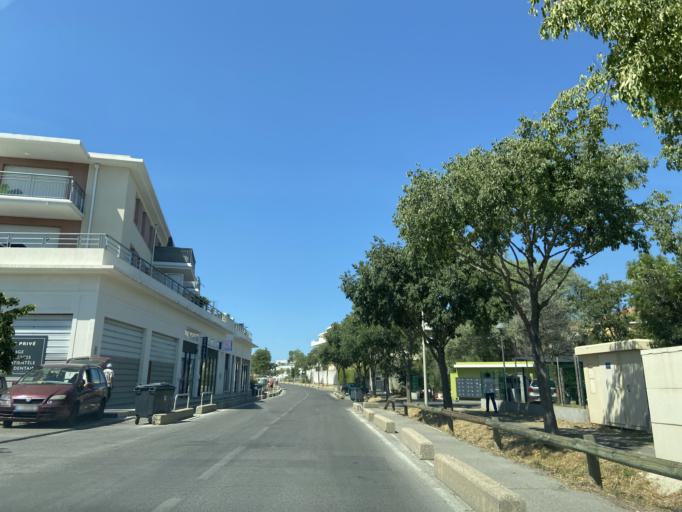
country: FR
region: Provence-Alpes-Cote d'Azur
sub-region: Departement des Bouches-du-Rhone
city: Plan-de-Cuques
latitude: 43.3442
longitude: 5.4418
